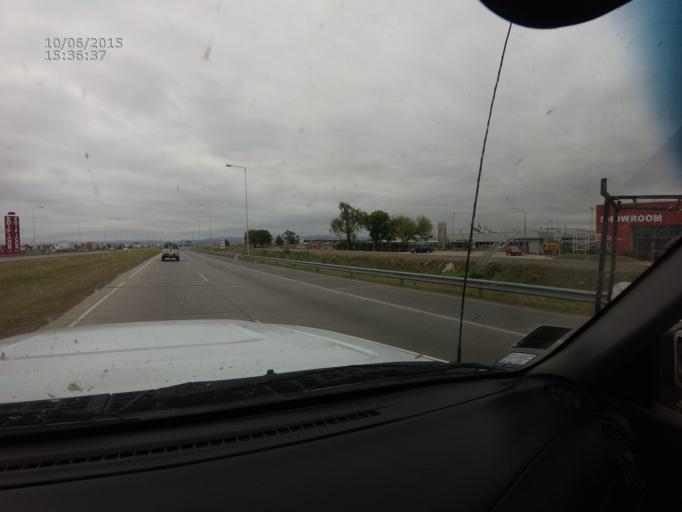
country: AR
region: Cordoba
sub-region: Departamento de Capital
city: Cordoba
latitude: -31.3549
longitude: -64.2103
